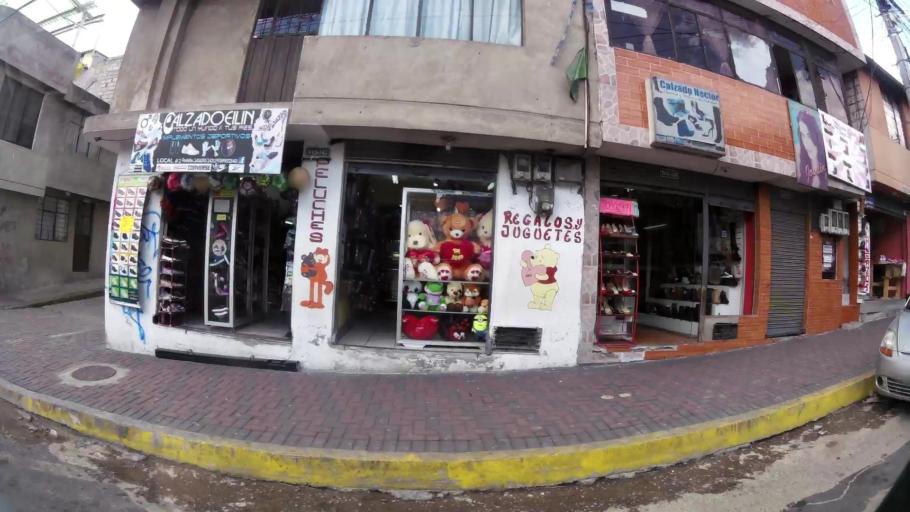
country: EC
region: Pichincha
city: Quito
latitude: -0.0929
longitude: -78.4529
